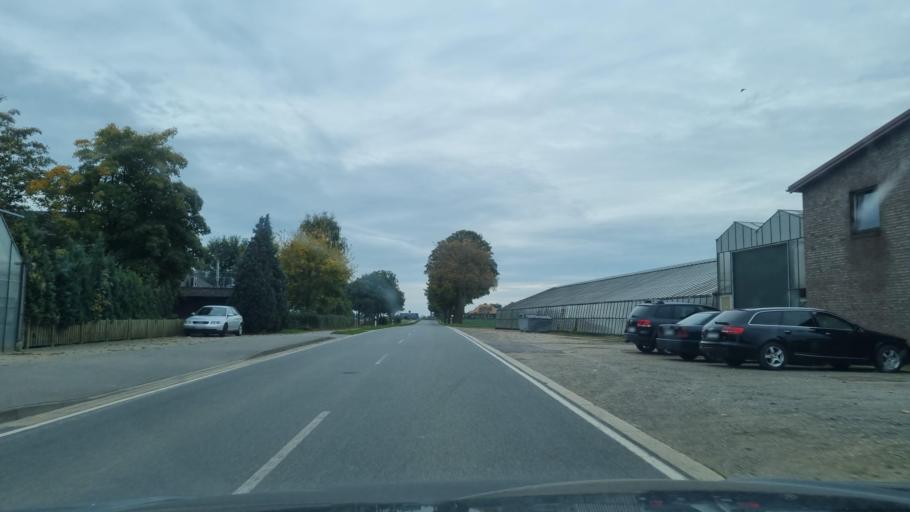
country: DE
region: North Rhine-Westphalia
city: Kalkar
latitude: 51.7251
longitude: 6.2875
